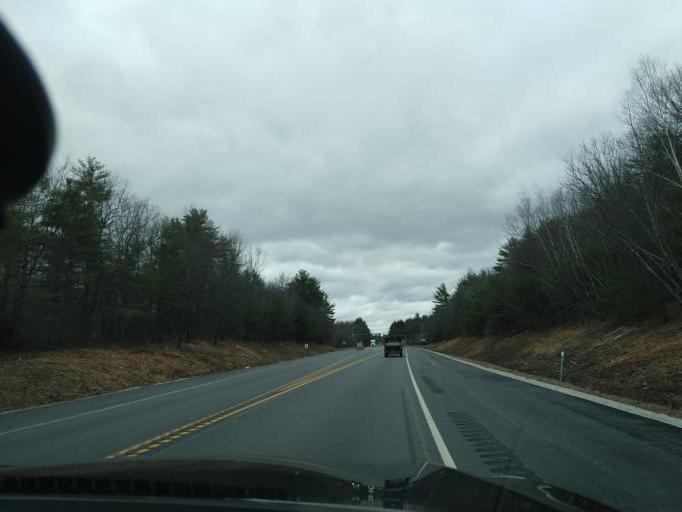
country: US
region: New Hampshire
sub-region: Rockingham County
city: Kingston
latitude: 42.9278
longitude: -71.0450
